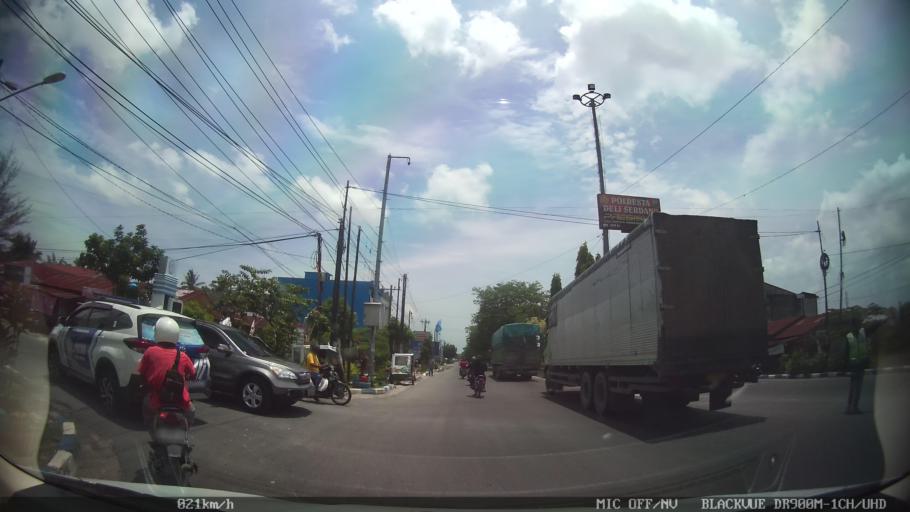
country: ID
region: North Sumatra
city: Percut
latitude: 3.5522
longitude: 98.8566
